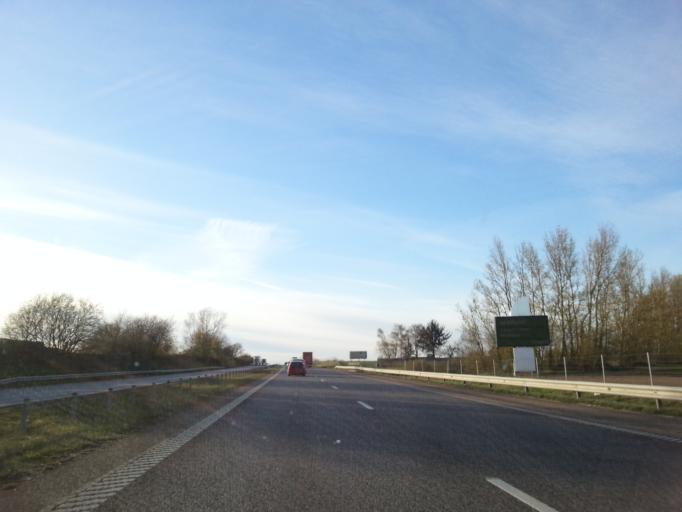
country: SE
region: Halland
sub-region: Halmstads Kommun
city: Paarp
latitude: 56.5971
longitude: 12.9324
